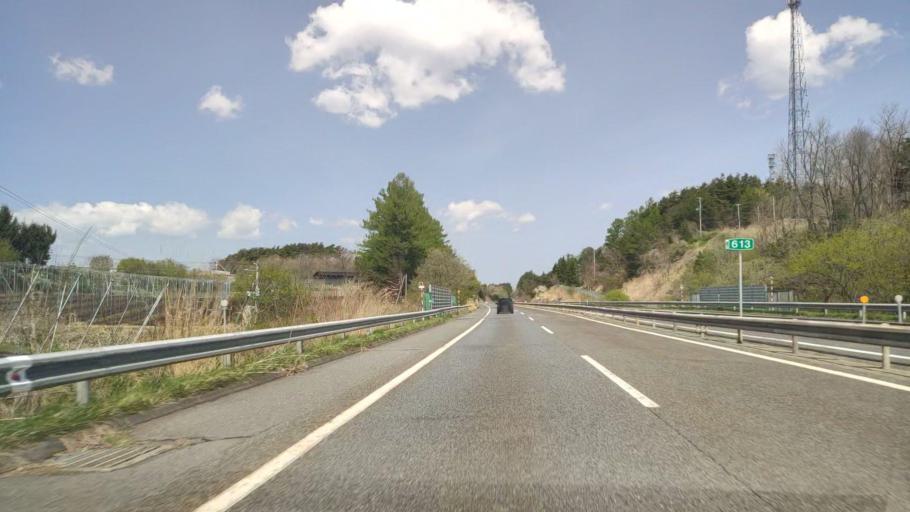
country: JP
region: Aomori
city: Hachinohe
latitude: 40.3399
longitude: 141.4510
